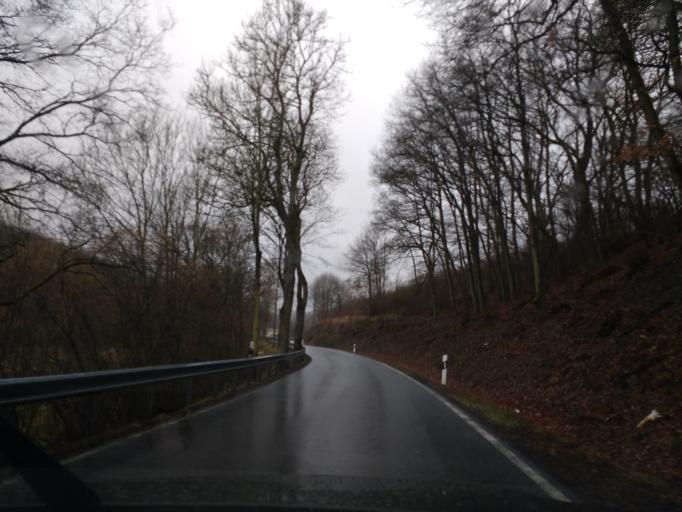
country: DE
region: Rheinland-Pfalz
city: Hilscheid
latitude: 49.7394
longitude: 6.9938
